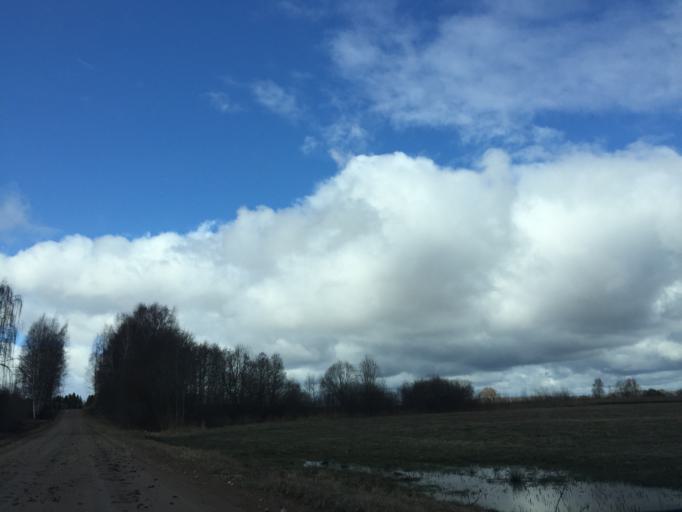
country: LV
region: Akniste
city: Akniste
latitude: 56.0939
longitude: 25.9900
